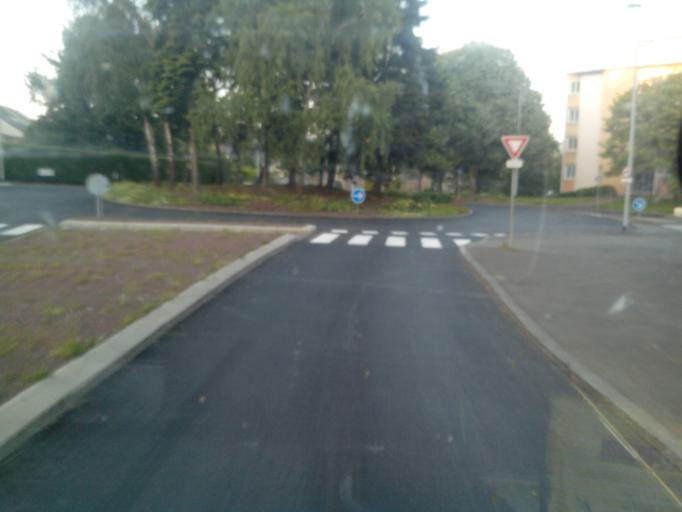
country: FR
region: Brittany
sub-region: Departement d'Ille-et-Vilaine
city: Fougeres
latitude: 48.3658
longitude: -1.1884
